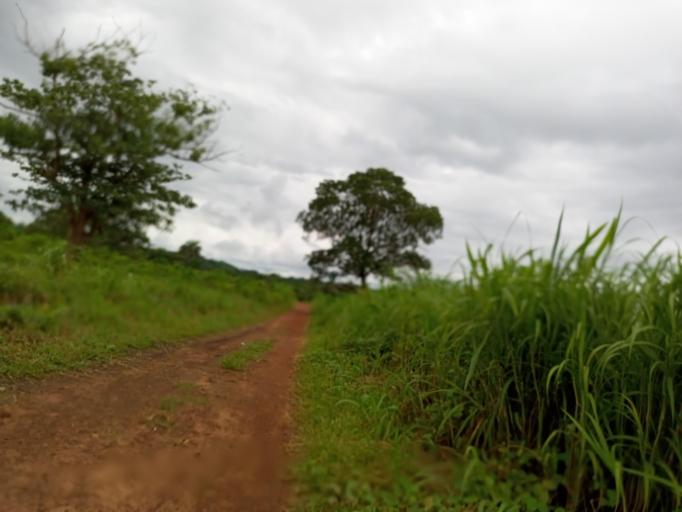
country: SL
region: Northern Province
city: Kamakwie
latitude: 9.5052
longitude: -12.2661
